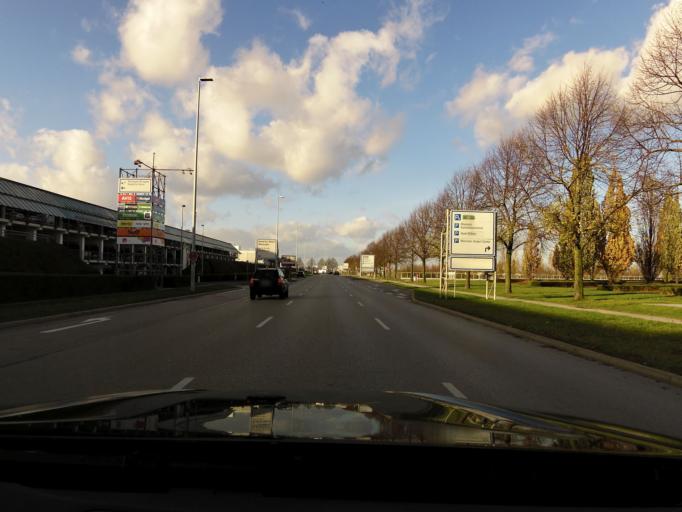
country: DE
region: Bavaria
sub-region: Upper Bavaria
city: Hallbergmoos
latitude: 48.3552
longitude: 11.7869
